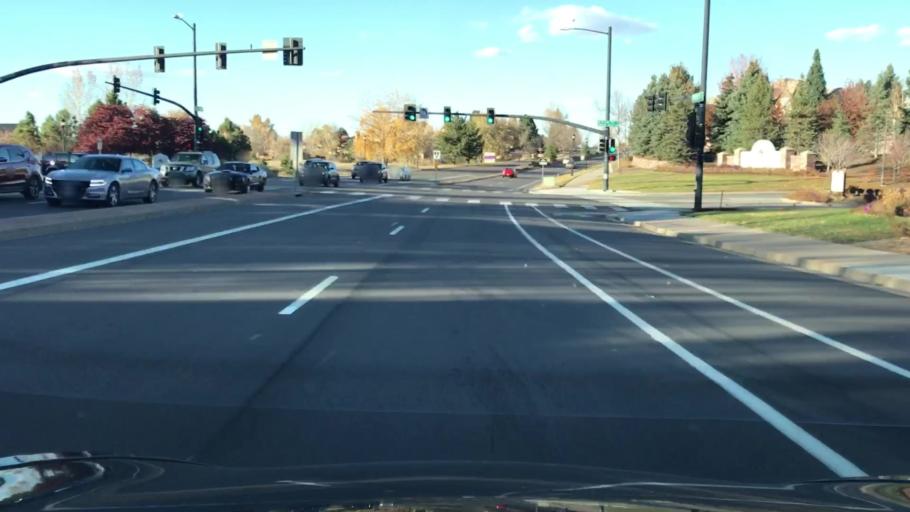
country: US
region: Colorado
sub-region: Adams County
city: Lone Tree
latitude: 39.5464
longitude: -104.8856
